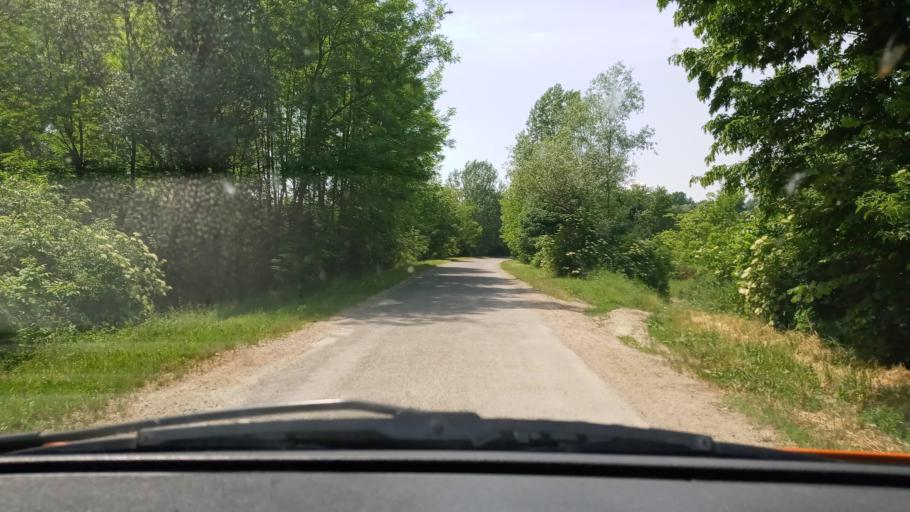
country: HU
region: Baranya
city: Sellye
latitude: 45.8064
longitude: 17.8856
